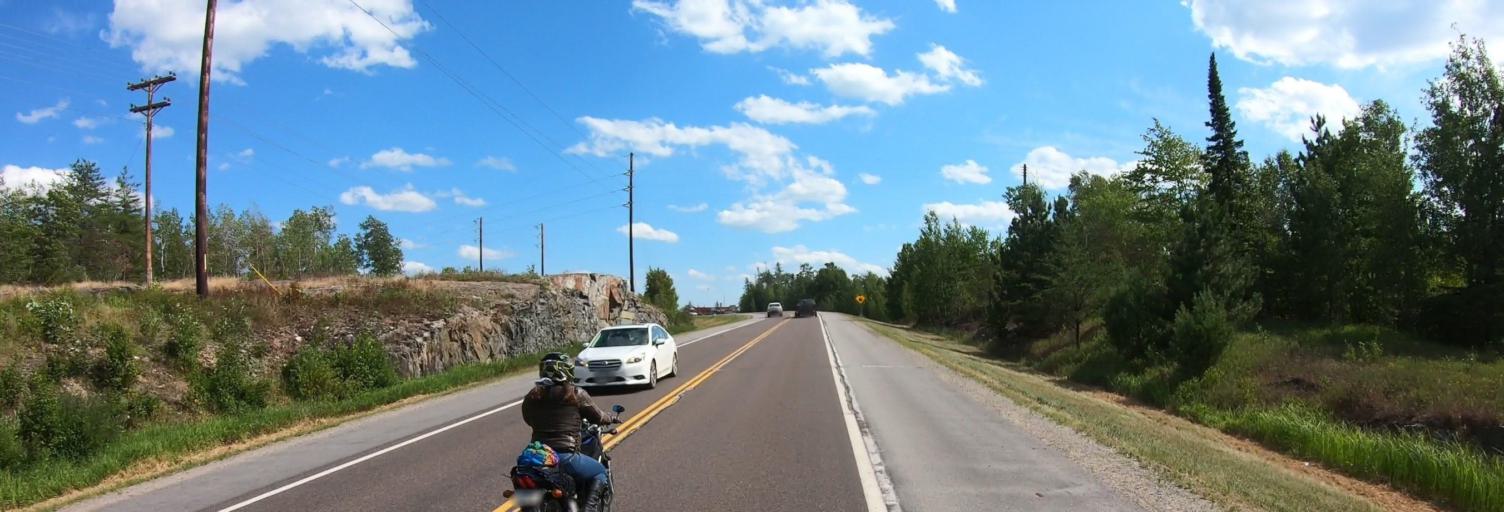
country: US
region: Minnesota
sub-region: Saint Louis County
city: Aurora
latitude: 47.7876
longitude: -92.3657
